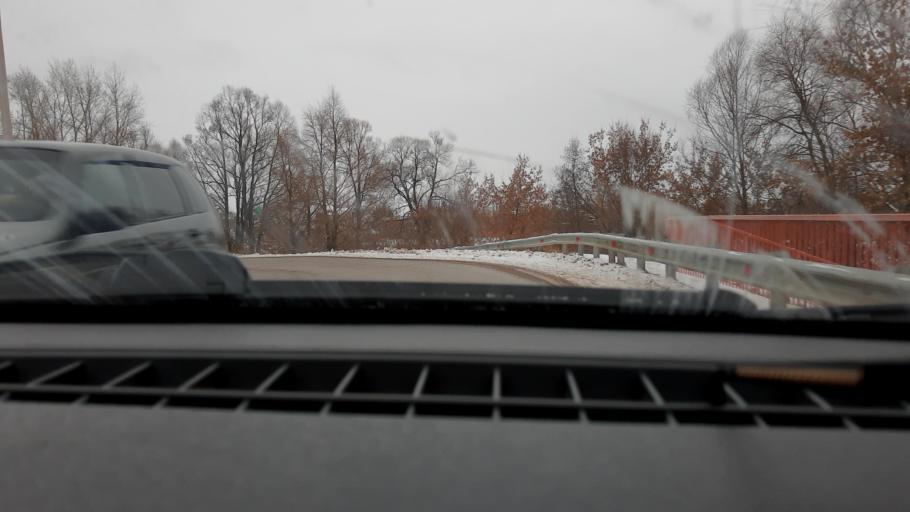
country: RU
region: Bashkortostan
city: Kabakovo
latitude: 54.7058
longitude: 56.2447
